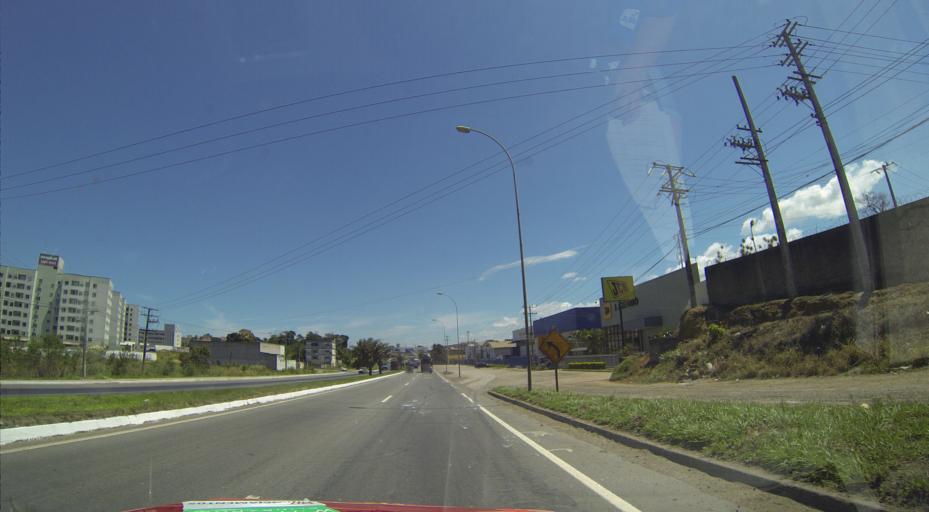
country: BR
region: Espirito Santo
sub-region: Serra
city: Serra
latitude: -20.1839
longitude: -40.2667
